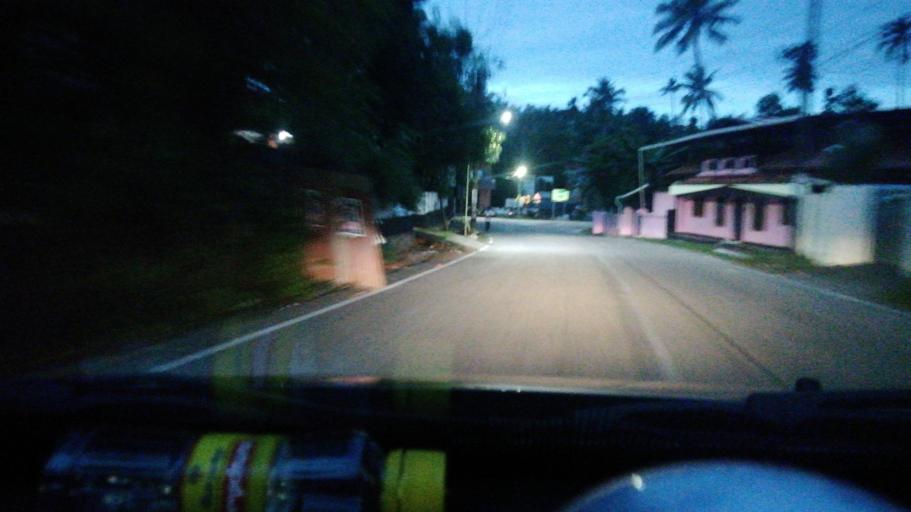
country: IN
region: Kerala
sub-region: Thiruvananthapuram
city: Paravur
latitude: 8.8118
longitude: 76.6736
